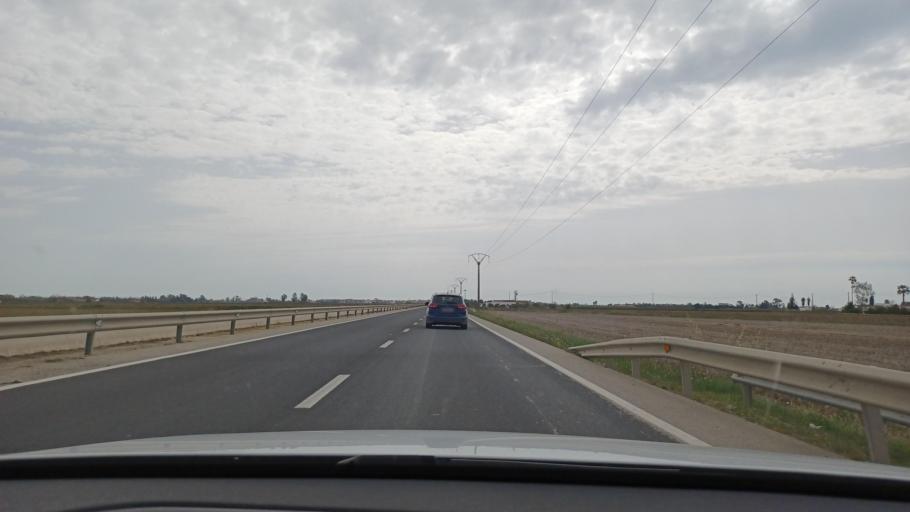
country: ES
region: Catalonia
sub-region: Provincia de Tarragona
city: Deltebre
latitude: 40.7088
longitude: 0.6868
